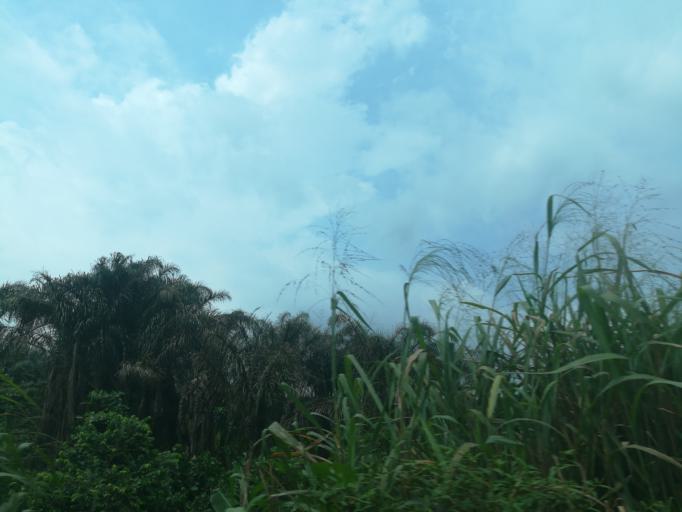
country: NG
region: Lagos
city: Ikorodu
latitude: 6.6717
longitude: 3.6652
